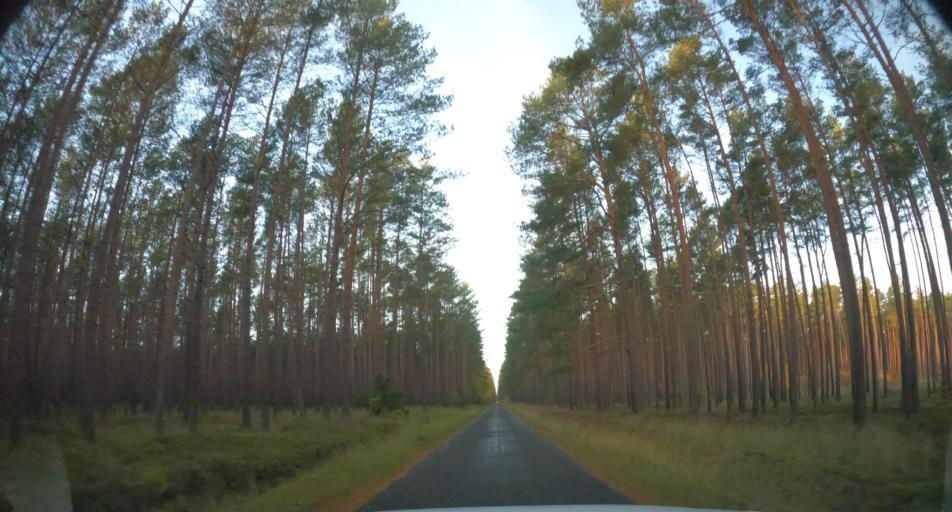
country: PL
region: West Pomeranian Voivodeship
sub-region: Powiat policki
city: Nowe Warpno
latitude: 53.6443
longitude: 14.3407
